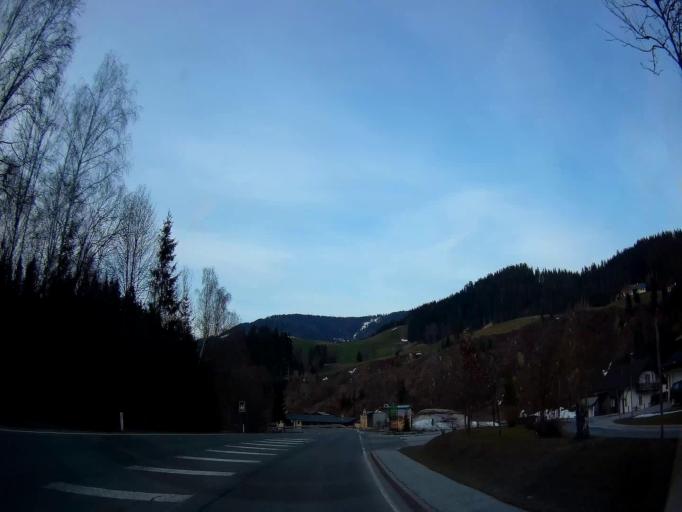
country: AT
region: Salzburg
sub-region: Politischer Bezirk Hallein
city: Abtenau
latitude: 47.5308
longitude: 13.4248
